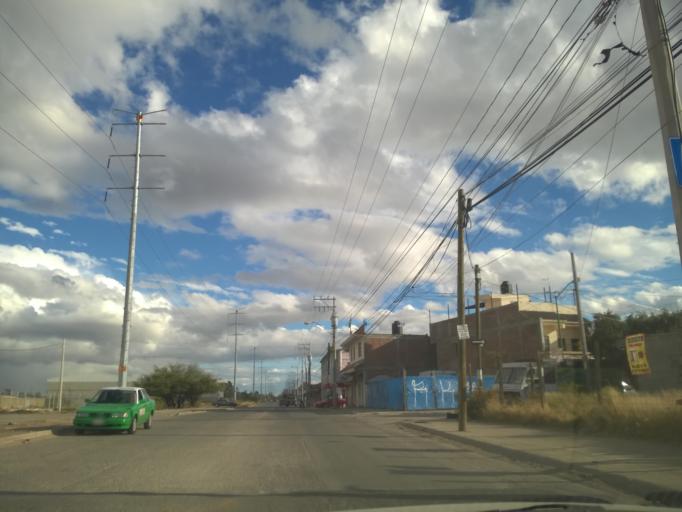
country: MX
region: Guanajuato
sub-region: Leon
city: Fraccionamiento Paraiso Real
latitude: 21.0744
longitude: -101.6150
